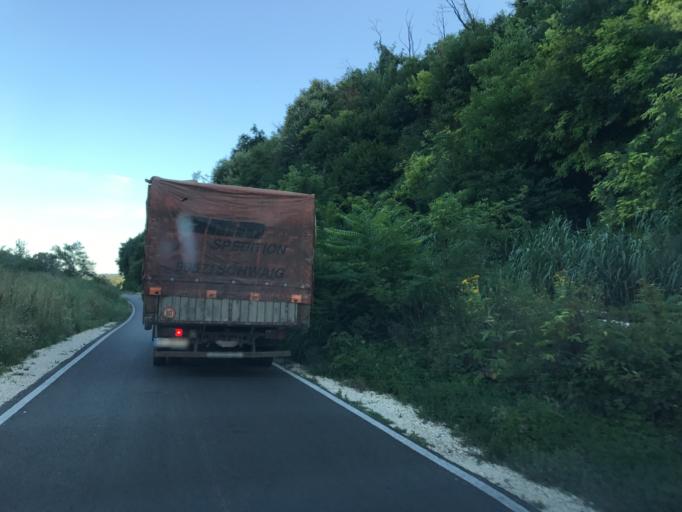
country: BG
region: Vidin
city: Bregovo
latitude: 44.1368
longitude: 22.6026
